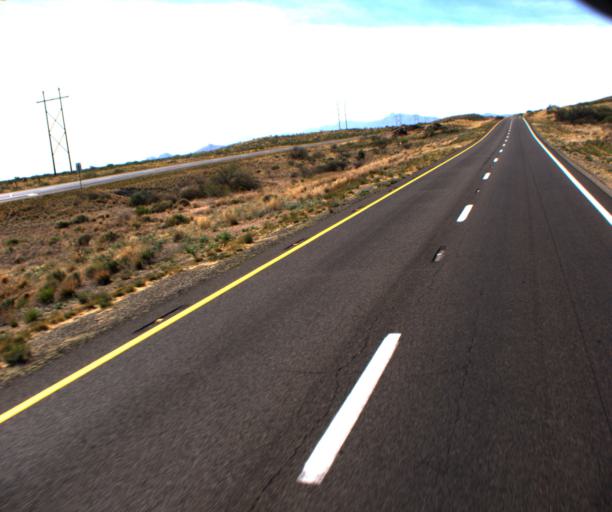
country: US
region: Arizona
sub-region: Graham County
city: Swift Trail Junction
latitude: 32.5222
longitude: -109.6741
